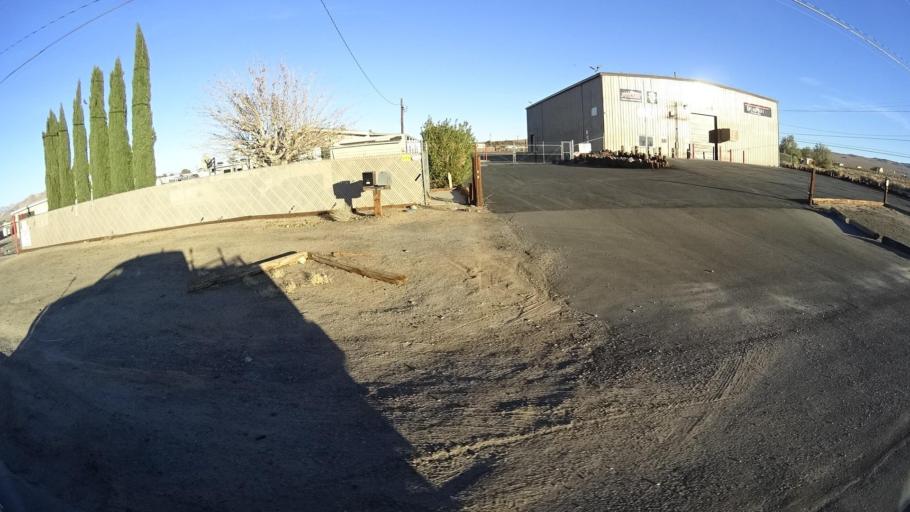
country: US
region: California
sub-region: Kern County
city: Ridgecrest
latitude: 35.6086
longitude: -117.6525
